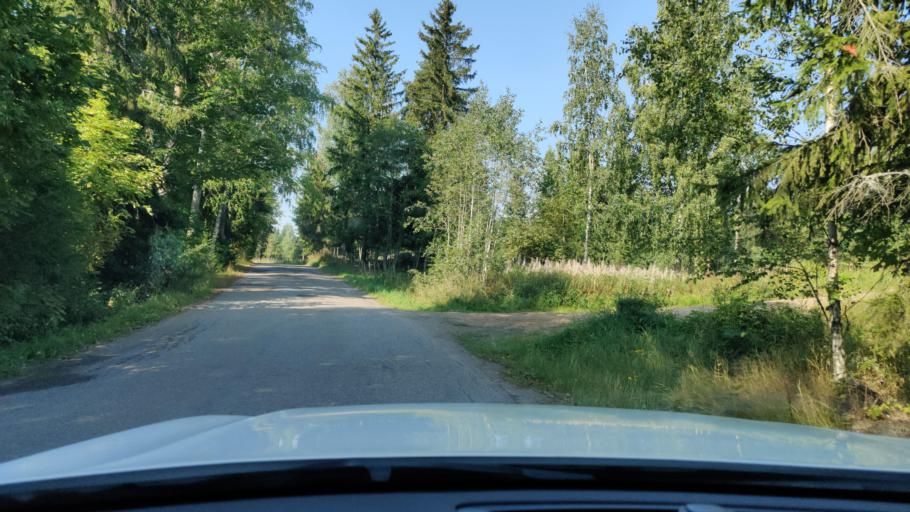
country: FI
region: Haeme
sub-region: Haemeenlinna
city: Tervakoski
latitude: 60.6770
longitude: 24.6242
